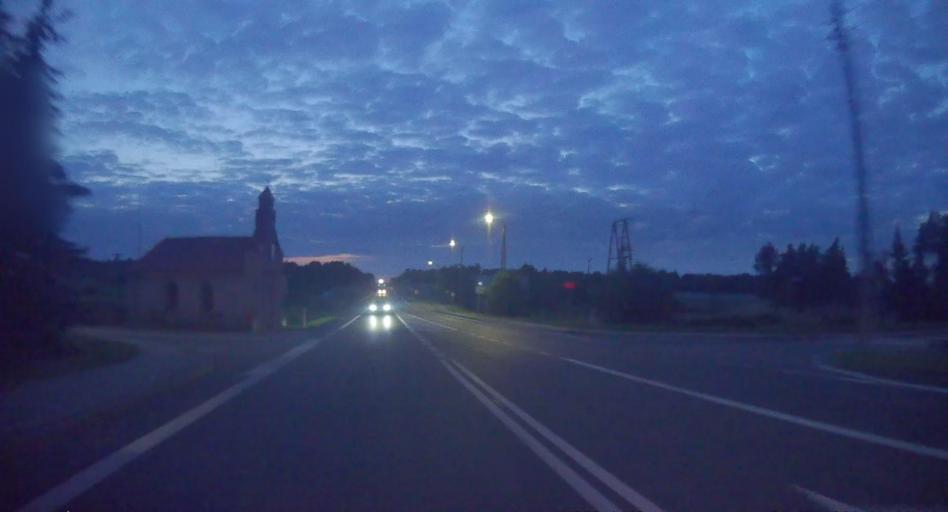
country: PL
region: Silesian Voivodeship
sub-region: Powiat klobucki
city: Kamyk
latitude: 50.8584
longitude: 19.0276
